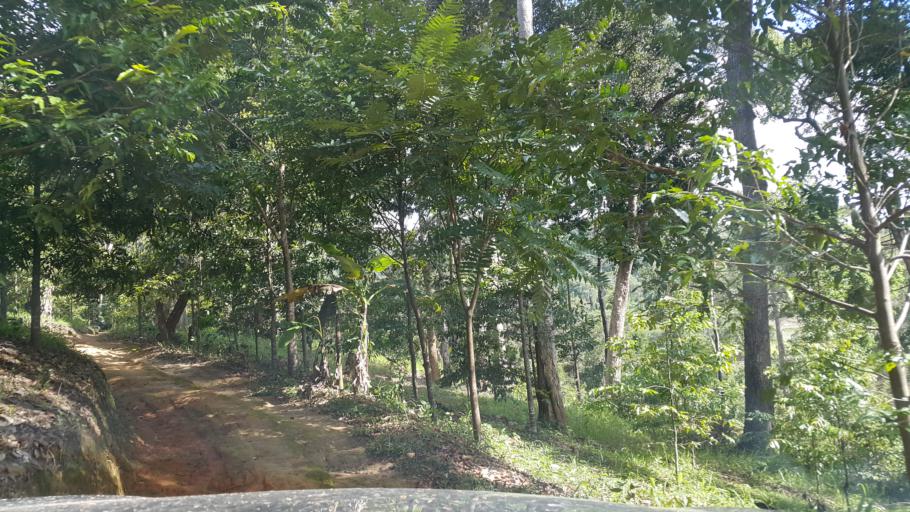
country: TH
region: Loei
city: Na Haeo
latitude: 17.5549
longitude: 100.9556
